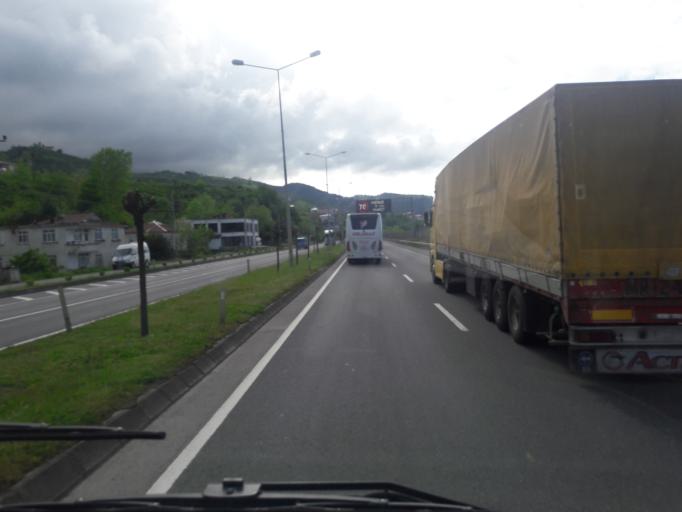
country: TR
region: Ordu
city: Gulyali
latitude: 40.9629
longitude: 38.0865
